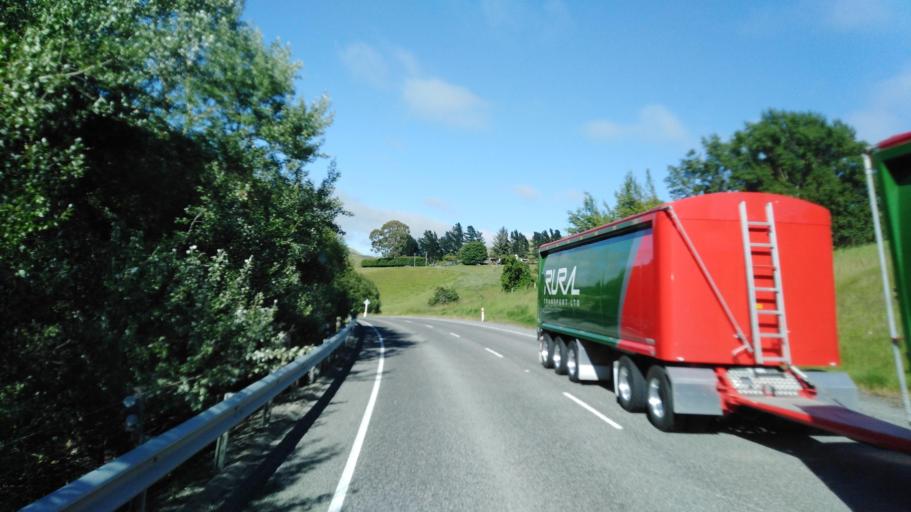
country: NZ
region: Canterbury
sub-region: Hurunui District
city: Amberley
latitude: -43.0051
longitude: 172.7065
